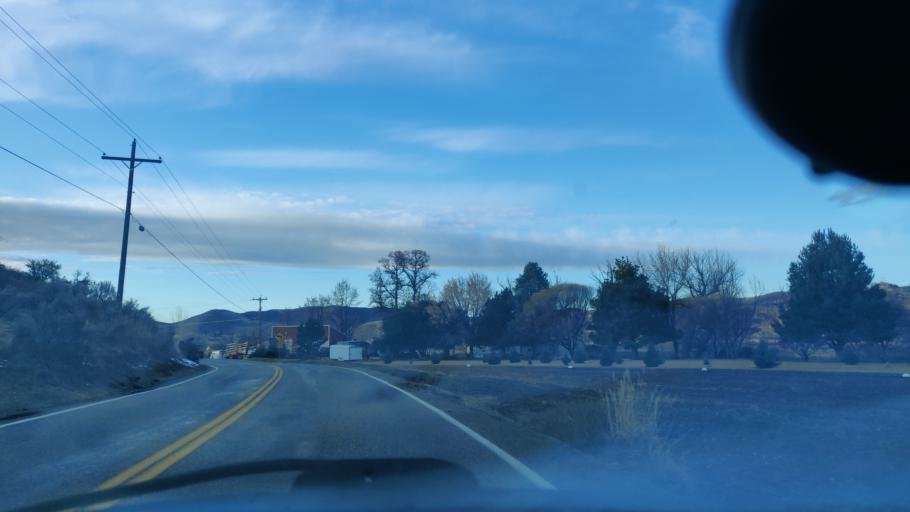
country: US
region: Idaho
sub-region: Ada County
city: Eagle
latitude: 43.7306
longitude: -116.2701
